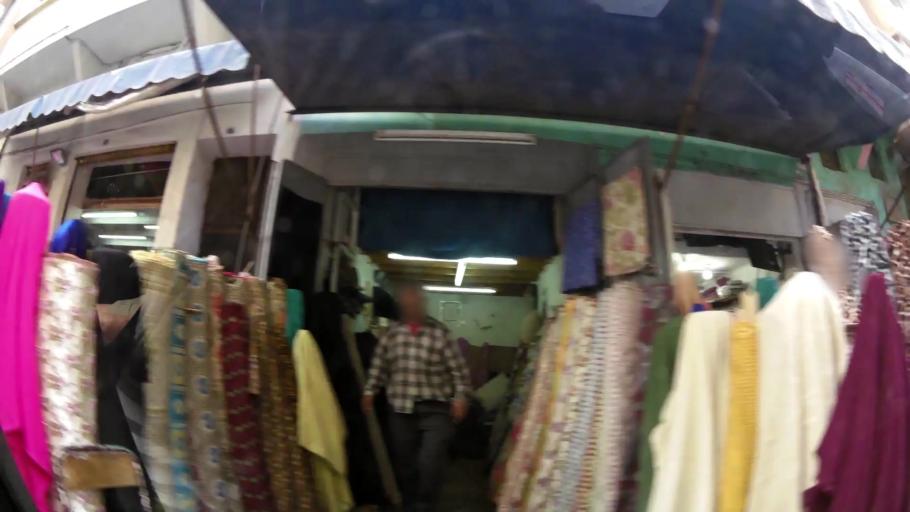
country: MA
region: Grand Casablanca
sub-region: Casablanca
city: Casablanca
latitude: 33.5675
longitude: -7.5874
